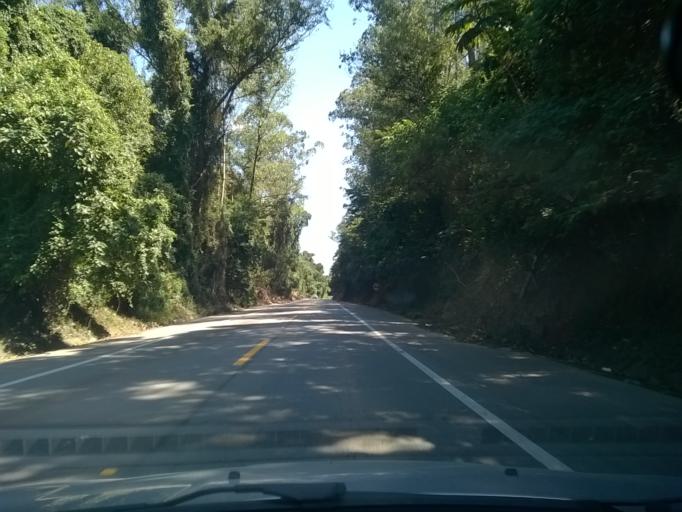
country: BR
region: Sao Paulo
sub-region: Varzea Paulista
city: Varzea Paulista
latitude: -23.2309
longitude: -46.8614
